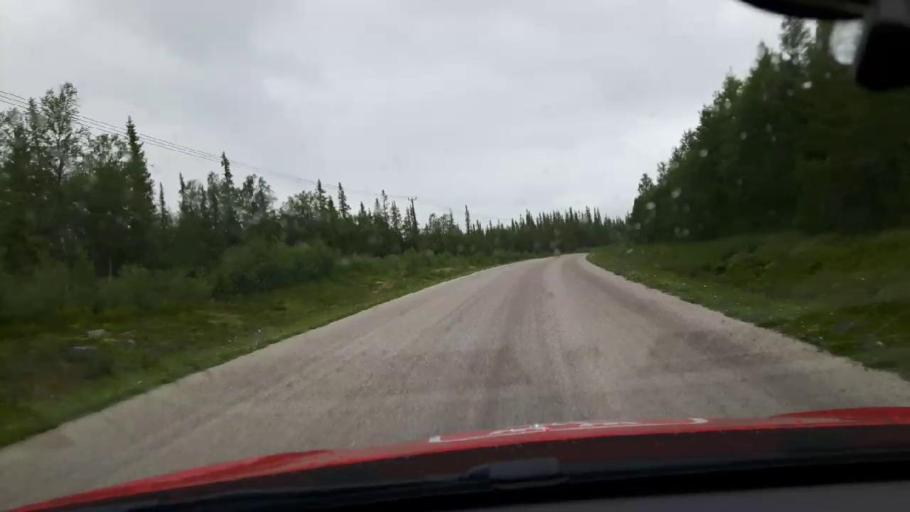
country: NO
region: Nord-Trondelag
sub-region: Meraker
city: Meraker
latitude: 63.2704
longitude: 12.3707
